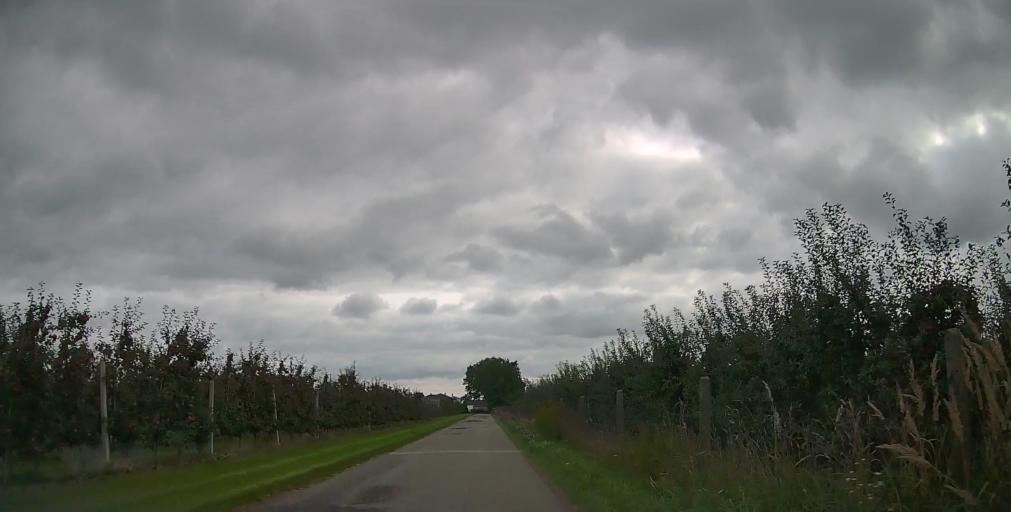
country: PL
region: Masovian Voivodeship
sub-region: Powiat grojecki
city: Goszczyn
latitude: 51.7614
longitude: 20.8709
